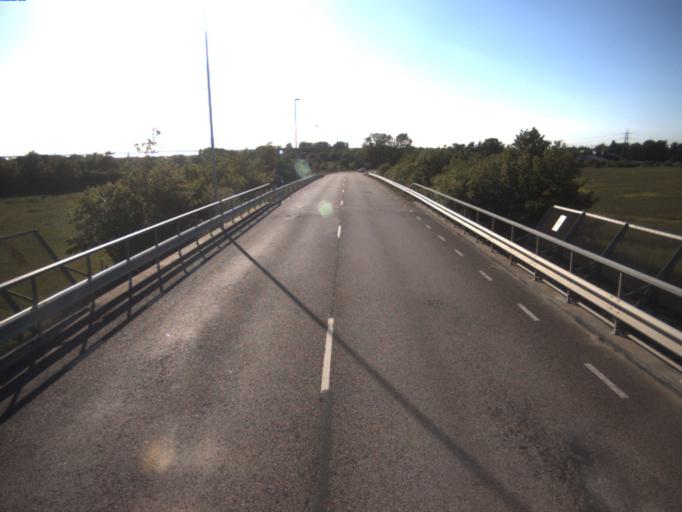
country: SE
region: Skane
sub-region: Helsingborg
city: Rydeback
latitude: 55.9705
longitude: 12.7828
